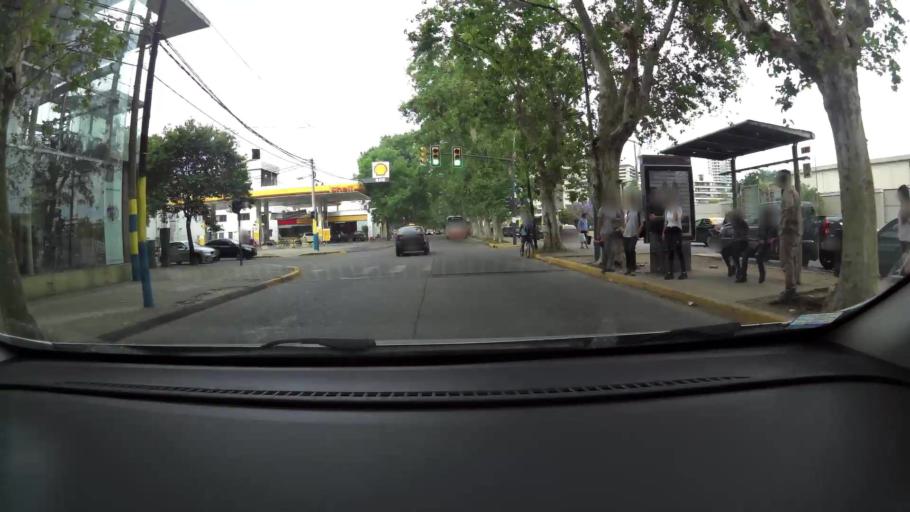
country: AR
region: Santa Fe
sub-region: Departamento de Rosario
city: Rosario
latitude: -32.9264
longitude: -60.6677
